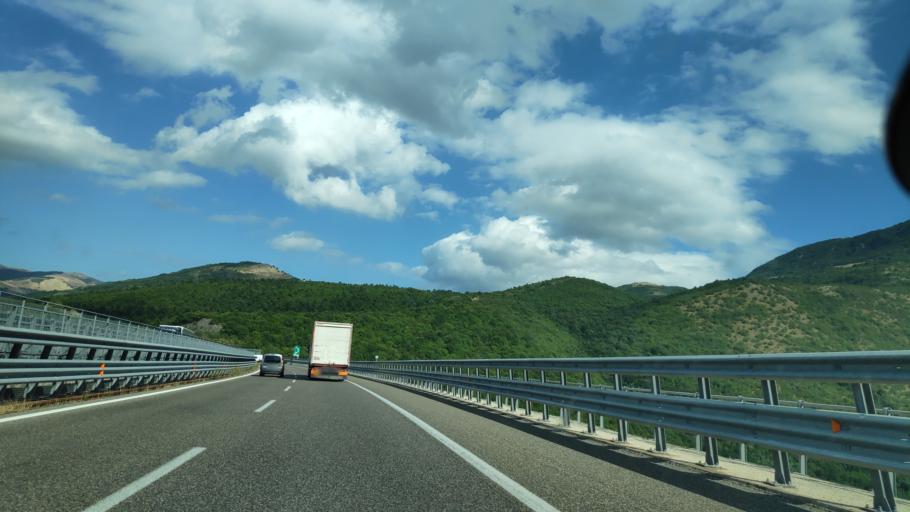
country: IT
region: Campania
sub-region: Provincia di Salerno
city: Pertosa
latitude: 40.5302
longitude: 15.4297
